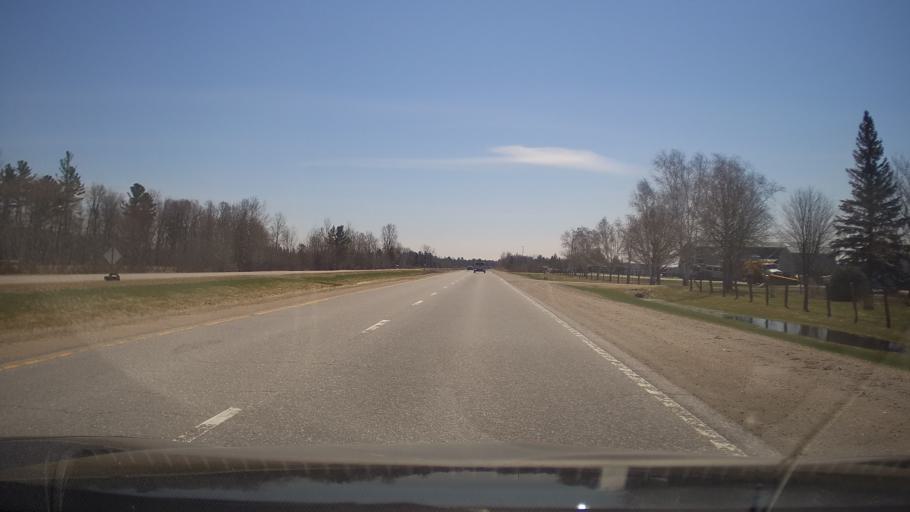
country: CA
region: Quebec
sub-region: Outaouais
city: Wakefield
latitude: 45.5219
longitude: -75.9905
